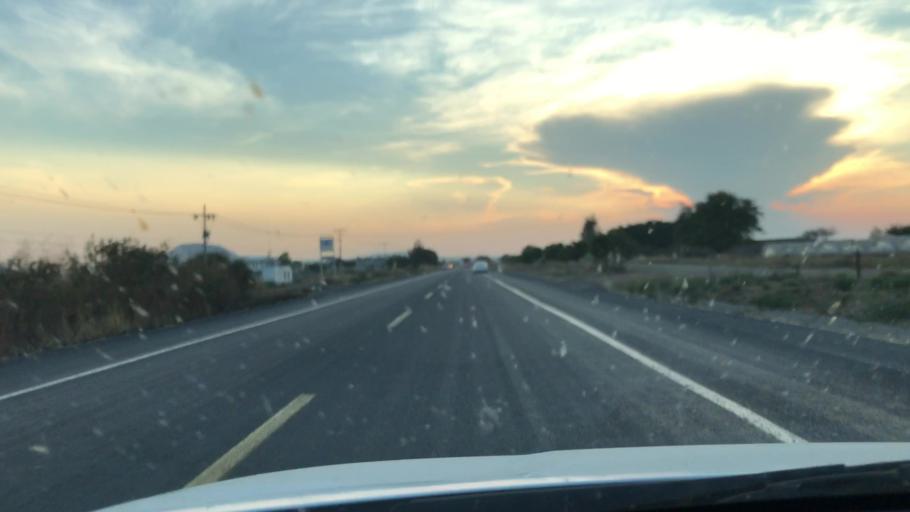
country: MX
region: Michoacan
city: Tanhuato de Guerrero
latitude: 20.3121
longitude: -102.3100
